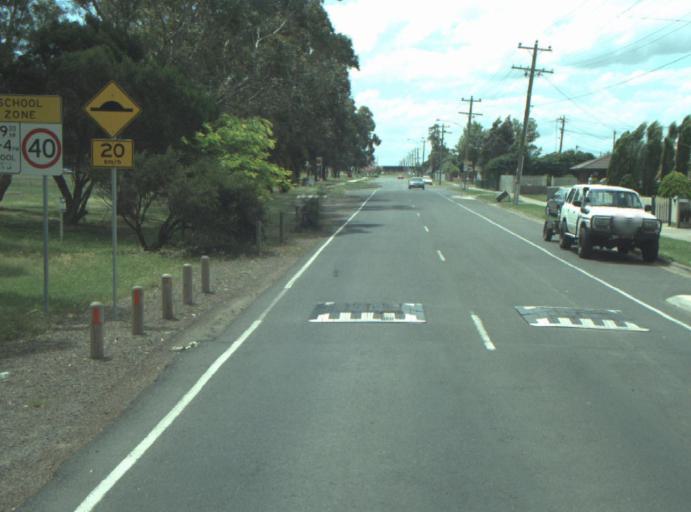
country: AU
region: Victoria
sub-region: Greater Geelong
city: Bell Park
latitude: -38.0667
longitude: 144.3675
